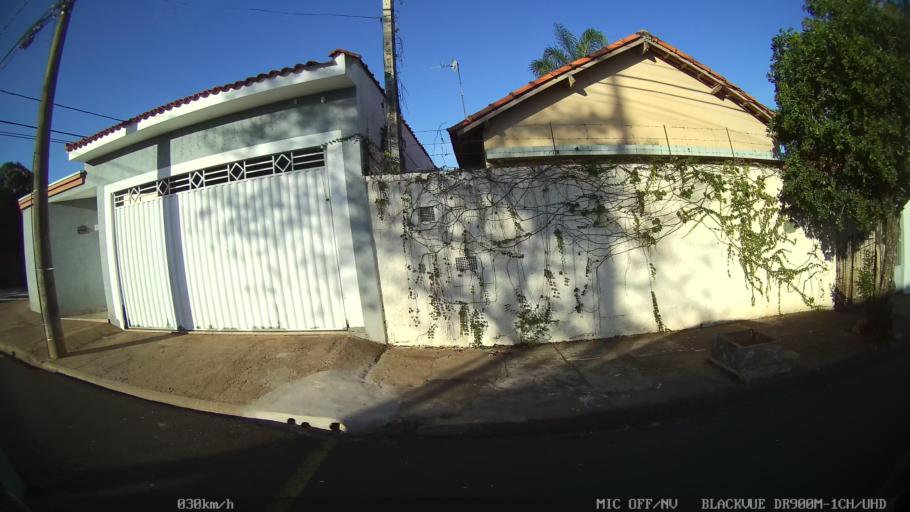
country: BR
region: Sao Paulo
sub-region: Franca
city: Franca
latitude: -20.5299
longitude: -47.3775
